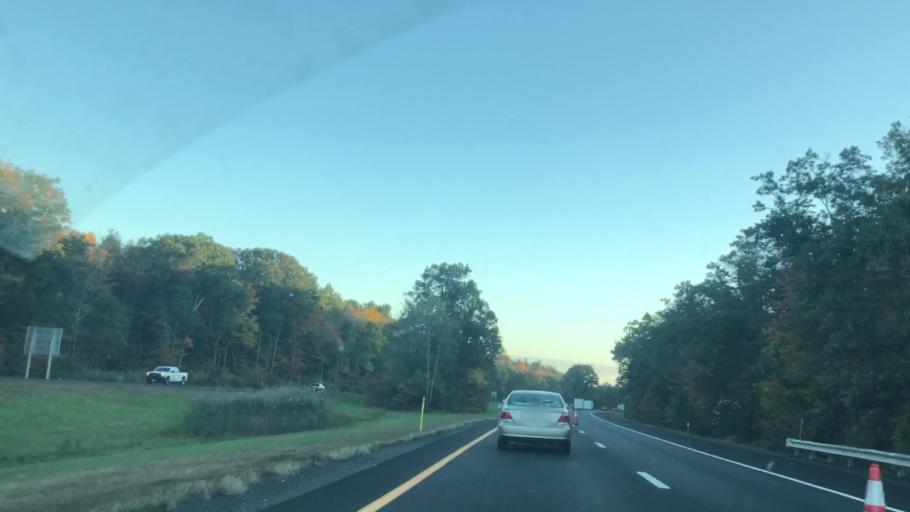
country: US
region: Massachusetts
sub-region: Franklin County
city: South Deerfield
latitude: 42.4926
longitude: -72.6165
